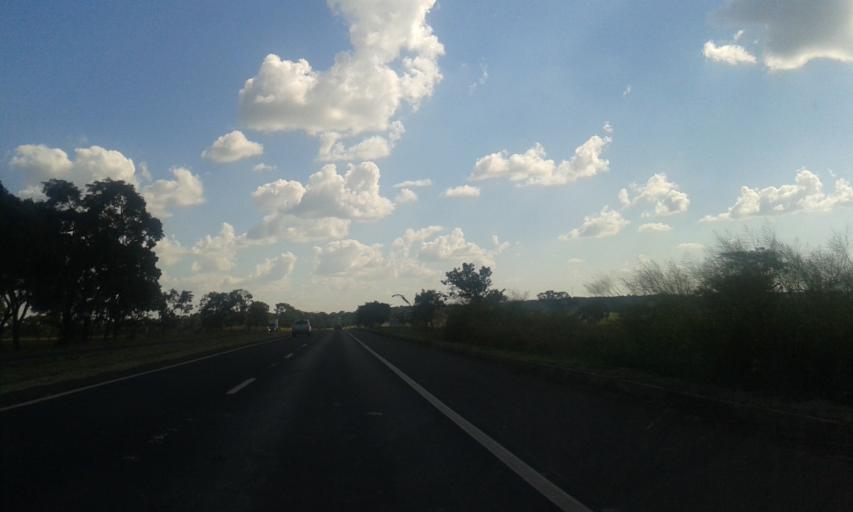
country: BR
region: Minas Gerais
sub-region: Monte Alegre De Minas
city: Monte Alegre de Minas
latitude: -18.8932
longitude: -48.6475
